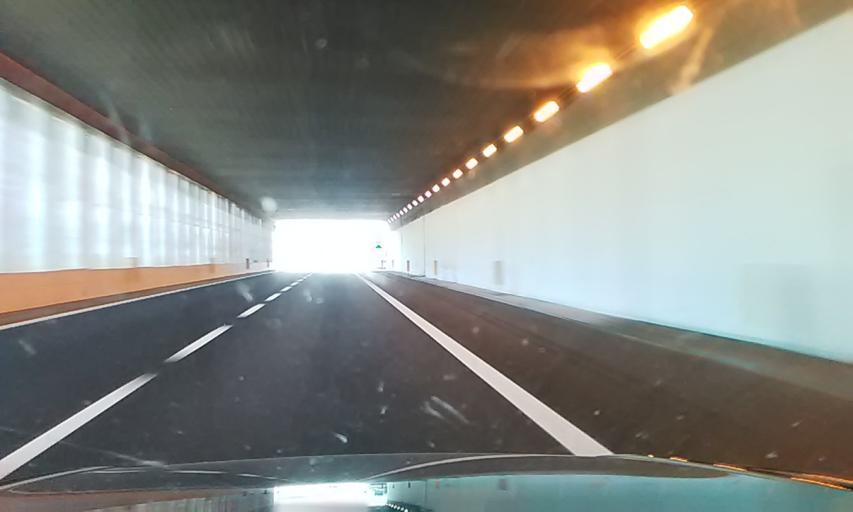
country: IT
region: Liguria
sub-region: Provincia di Savona
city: Villanova d'Albenga
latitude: 44.0460
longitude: 8.1464
